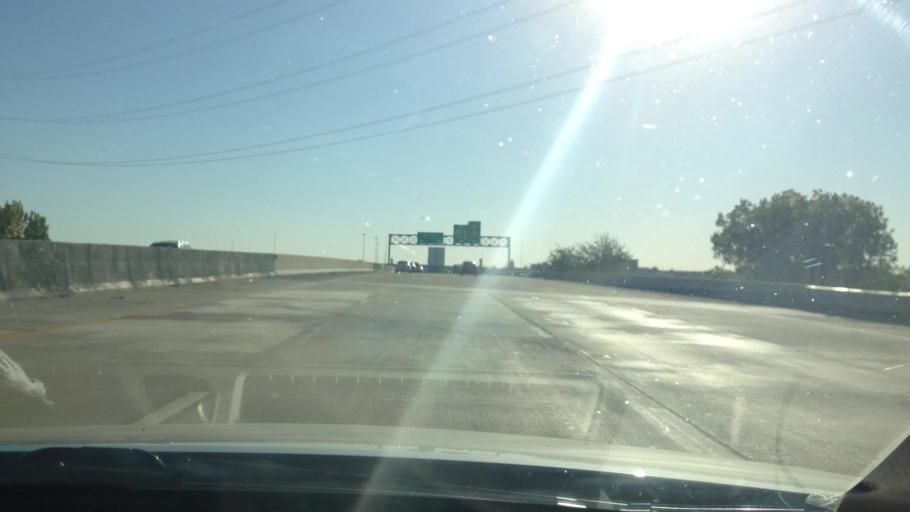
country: US
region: Kansas
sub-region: Johnson County
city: Olathe
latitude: 38.8631
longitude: -94.8059
